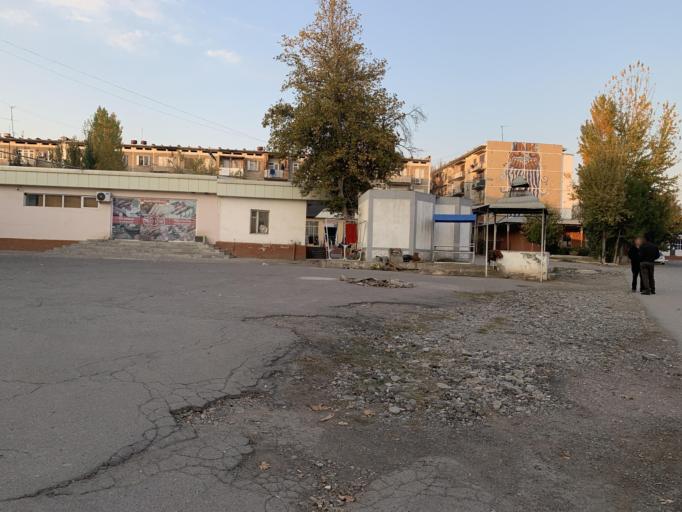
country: UZ
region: Namangan
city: Namangan Shahri
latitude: 41.0048
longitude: 71.5992
